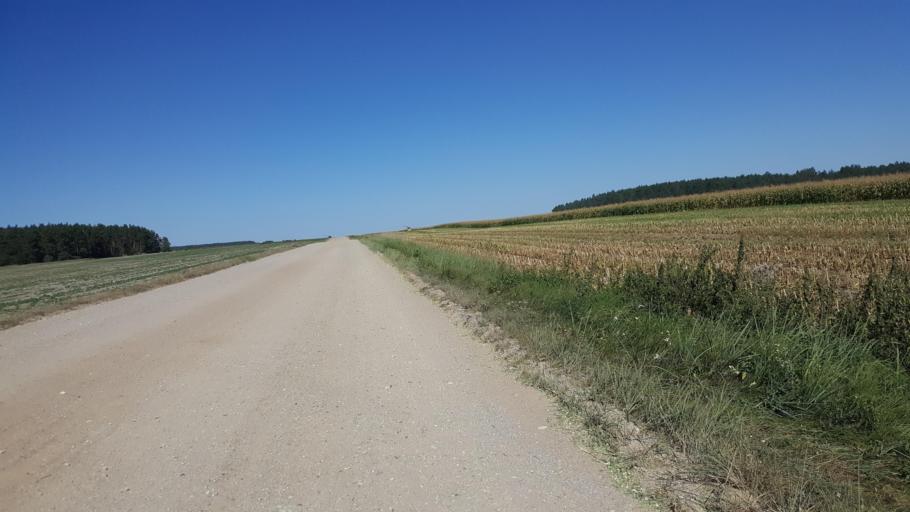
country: PL
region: Lublin Voivodeship
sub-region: Powiat bialski
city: Rokitno
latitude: 52.2176
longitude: 23.3981
